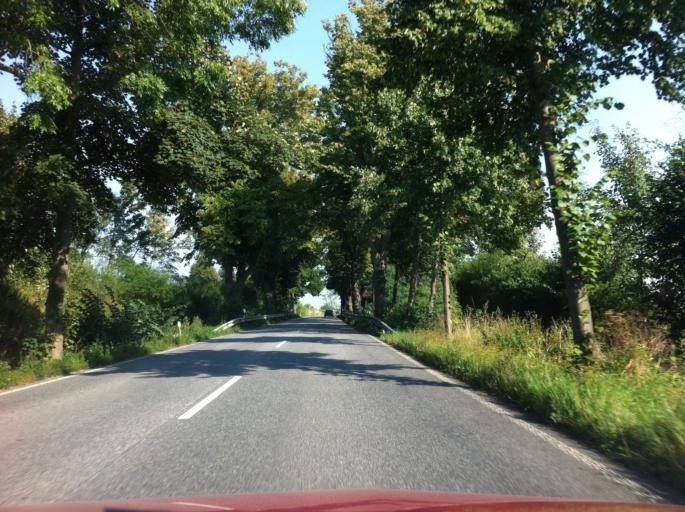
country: DE
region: Schleswig-Holstein
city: Wangels
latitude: 54.3007
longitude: 10.7622
